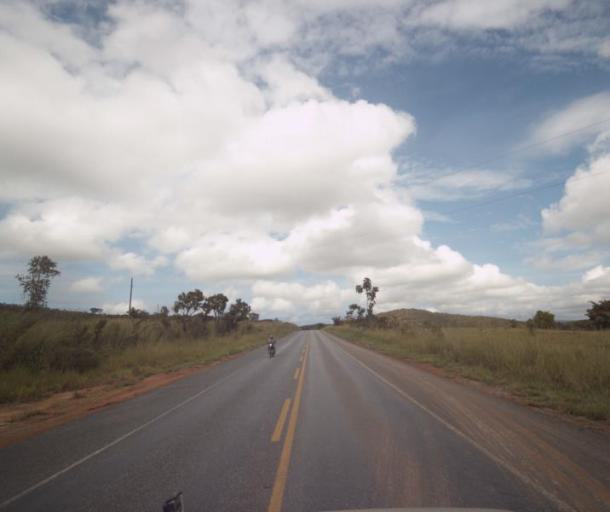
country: BR
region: Goias
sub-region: Pirenopolis
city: Pirenopolis
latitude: -15.6070
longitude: -48.6502
